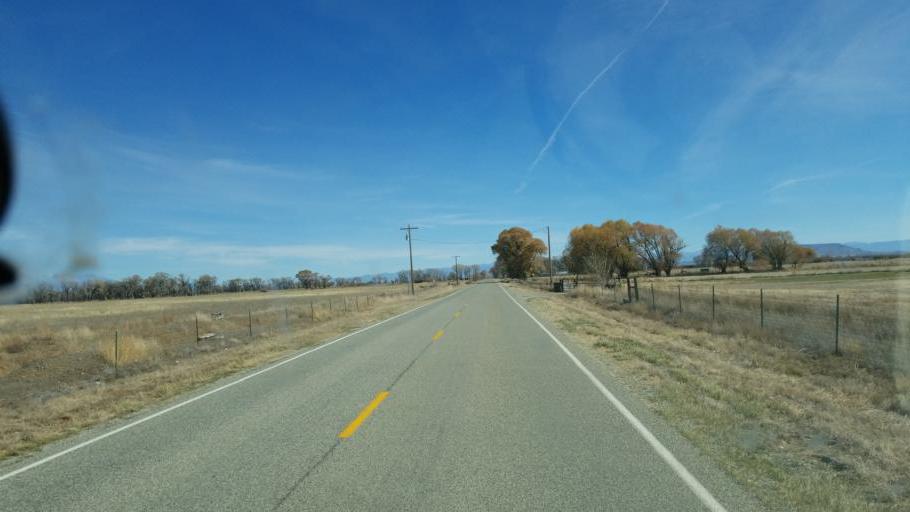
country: US
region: Colorado
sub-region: Conejos County
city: Conejos
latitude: 37.2834
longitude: -106.0541
